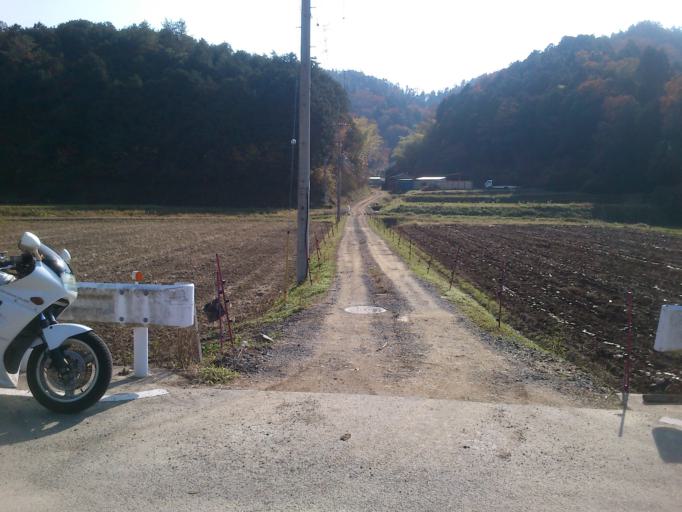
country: JP
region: Kyoto
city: Ayabe
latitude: 35.3670
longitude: 135.2671
